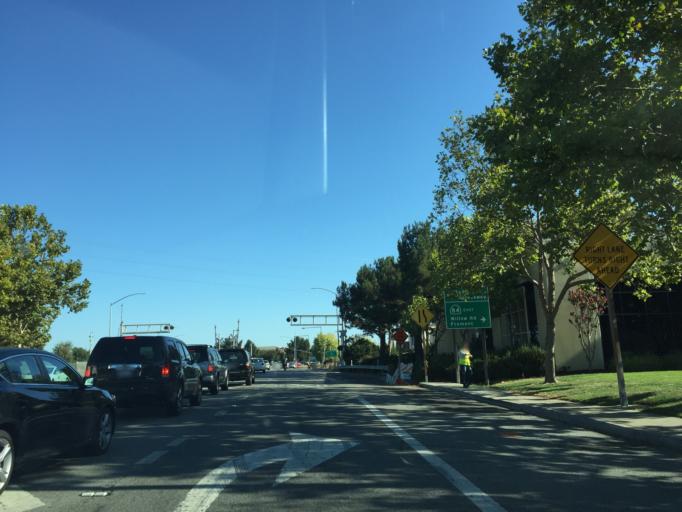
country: US
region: California
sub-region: San Mateo County
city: East Palo Alto
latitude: 37.4798
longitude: -122.1508
